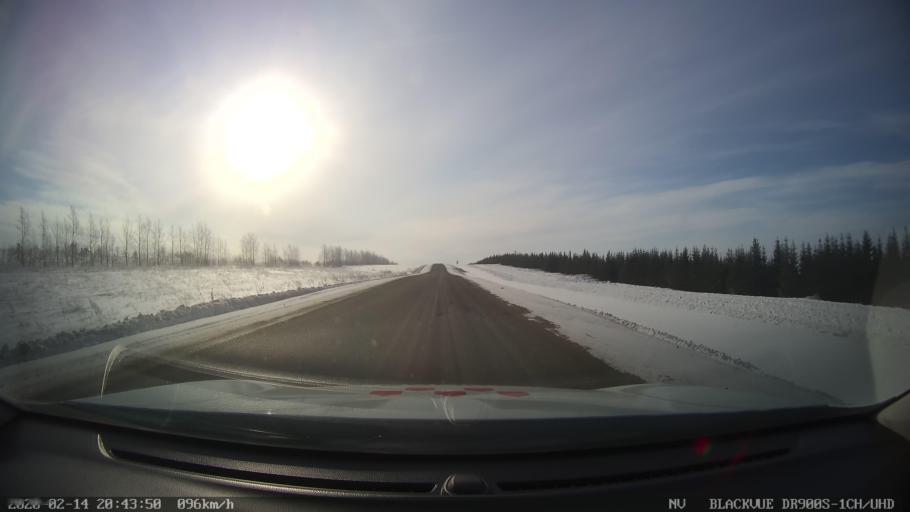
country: RU
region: Tatarstan
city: Kuybyshevskiy Zaton
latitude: 55.3029
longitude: 49.1478
